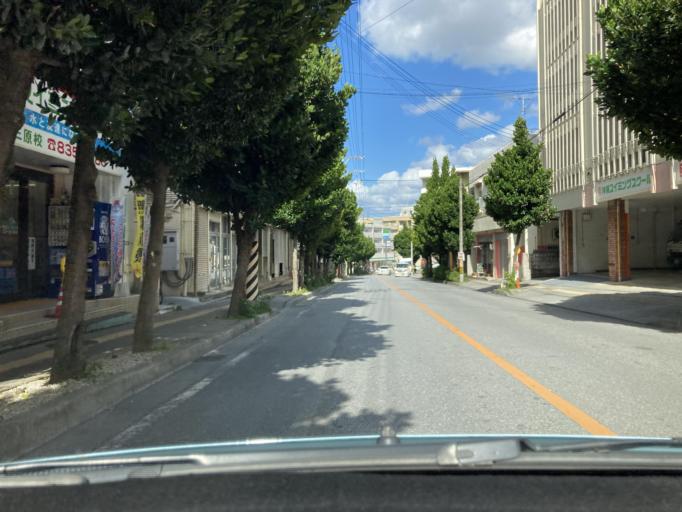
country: JP
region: Okinawa
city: Naha-shi
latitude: 26.2127
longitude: 127.6995
